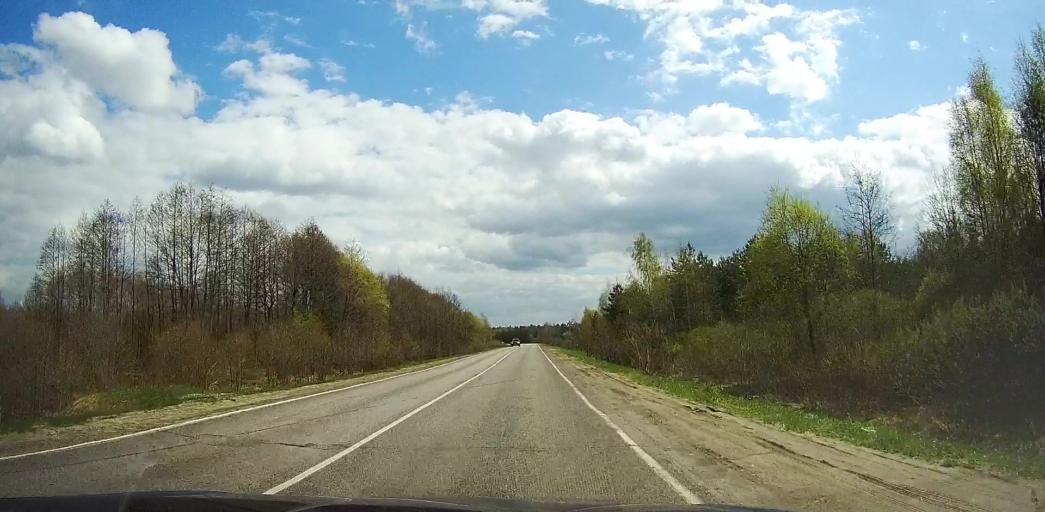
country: RU
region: Moskovskaya
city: Davydovo
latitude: 55.5488
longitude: 38.8068
